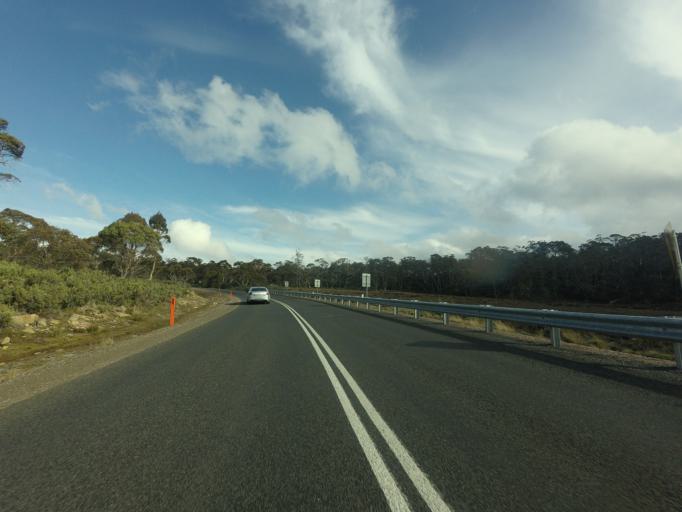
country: AU
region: Tasmania
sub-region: Meander Valley
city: Deloraine
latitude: -41.7872
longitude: 146.6928
